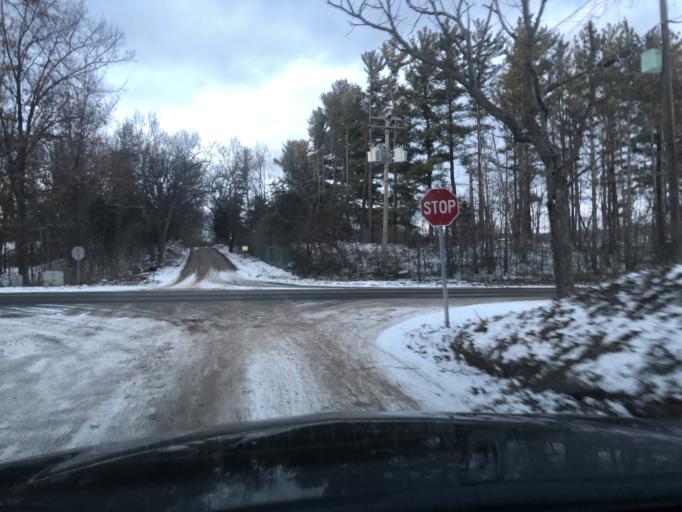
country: US
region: Michigan
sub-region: Oakland County
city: Milford
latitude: 42.5785
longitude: -83.6393
